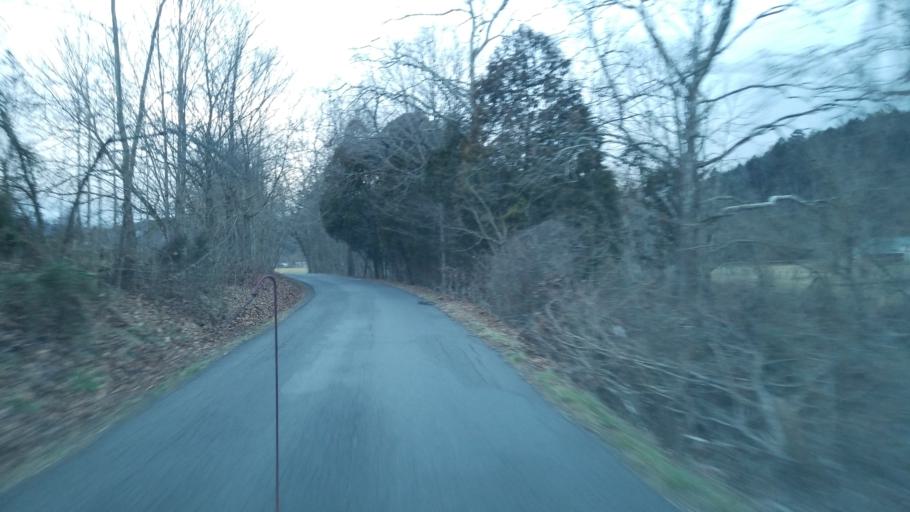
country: US
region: Virginia
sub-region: Pulaski County
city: Pulaski
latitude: 37.1617
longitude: -80.8619
